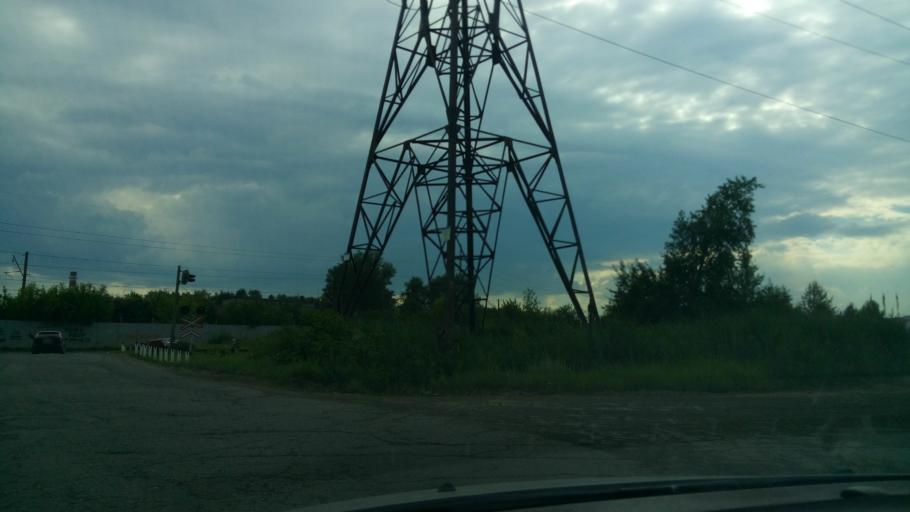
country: RU
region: Sverdlovsk
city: Yekaterinburg
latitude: 56.8871
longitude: 60.6627
